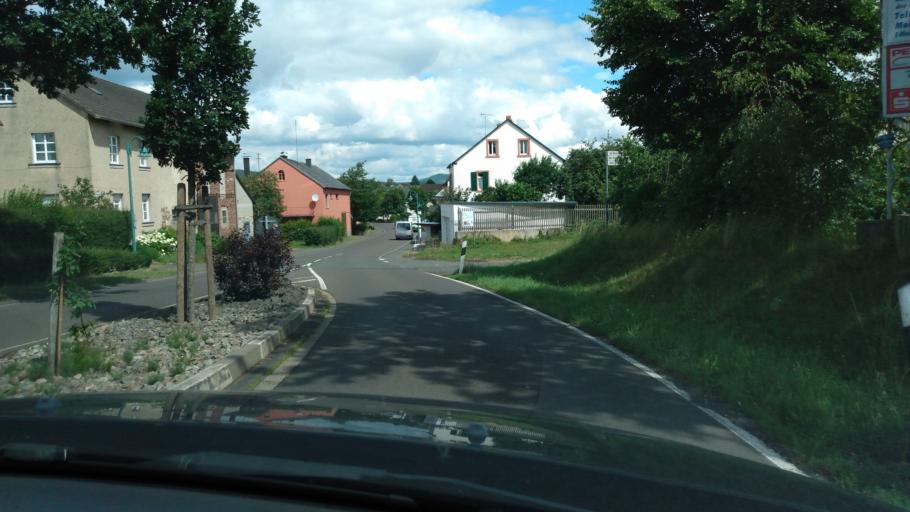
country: DE
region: Rheinland-Pfalz
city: Grosslittgen
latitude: 50.0227
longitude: 6.8020
